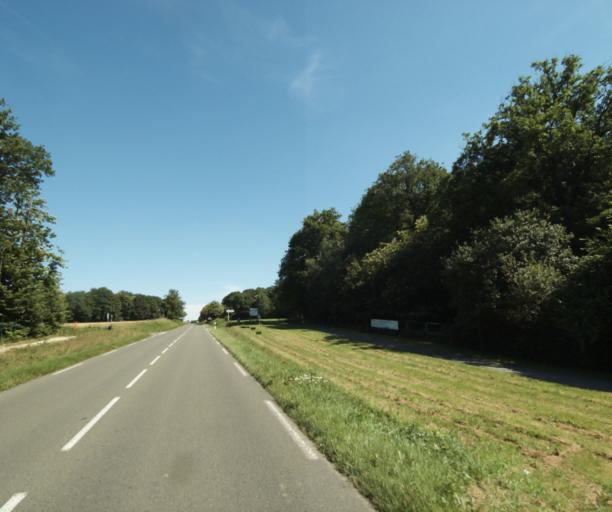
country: FR
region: Pays de la Loire
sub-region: Departement de la Mayenne
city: Laval
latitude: 48.0473
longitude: -0.7850
